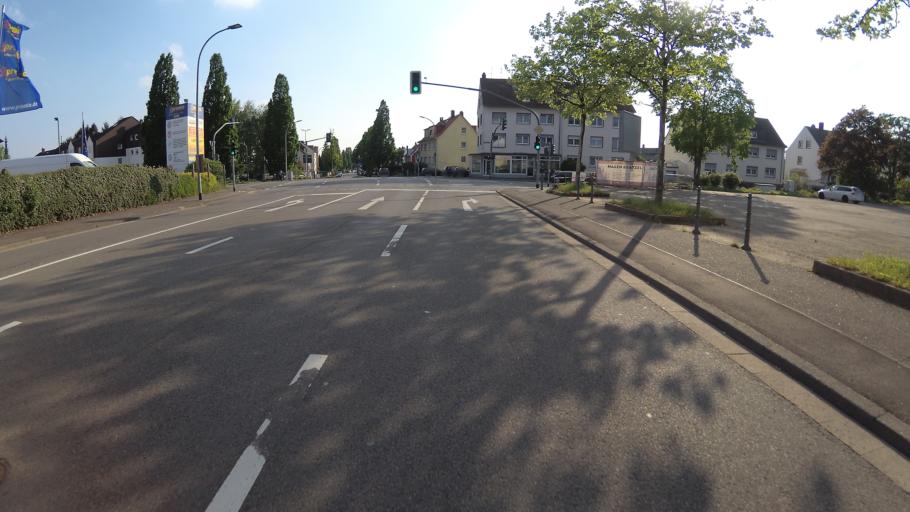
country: DE
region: Rheinland-Pfalz
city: Pirmasens
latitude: 49.1916
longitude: 7.5983
